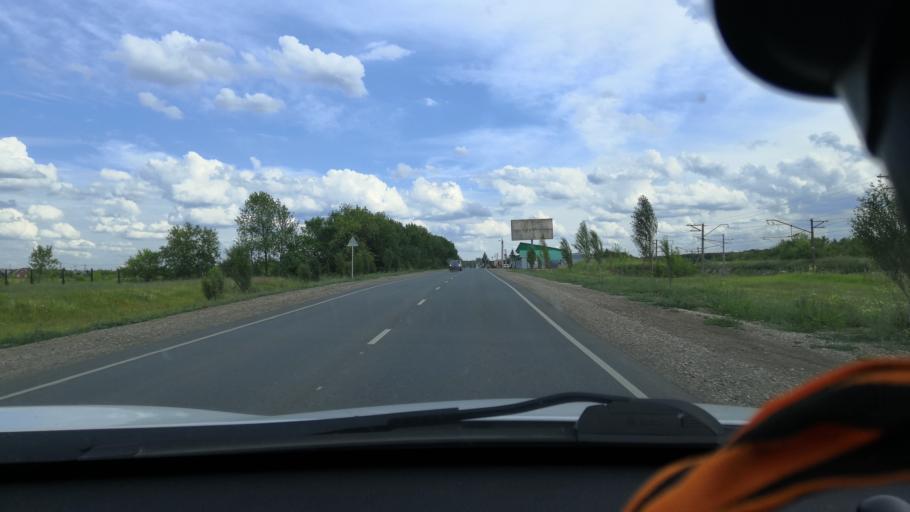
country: RU
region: Samara
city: Novosemeykino
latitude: 53.3825
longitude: 50.3341
